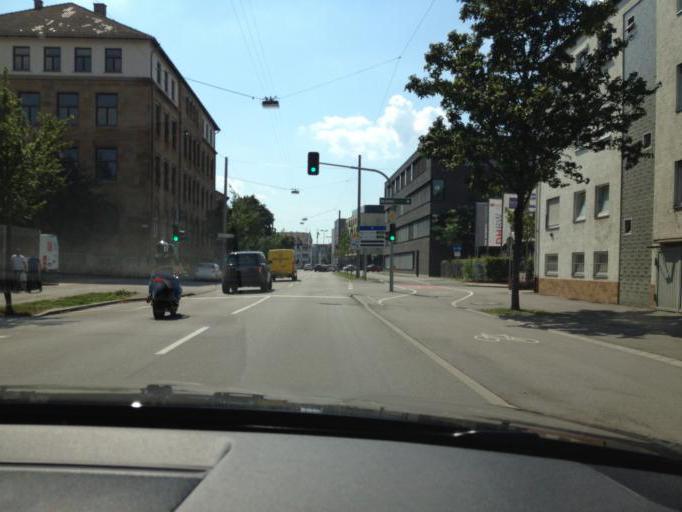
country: DE
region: Baden-Wuerttemberg
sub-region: Regierungsbezirk Stuttgart
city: Heilbronn
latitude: 49.1479
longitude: 9.2191
